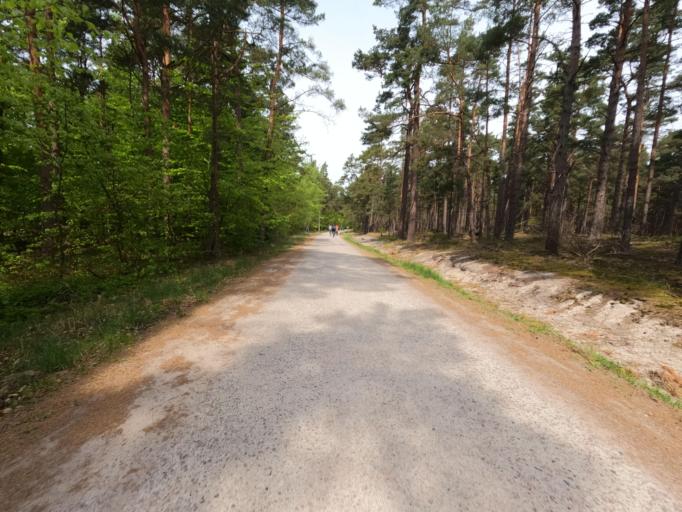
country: DE
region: Mecklenburg-Vorpommern
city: Ostseebad Prerow
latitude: 54.4673
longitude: 12.5090
